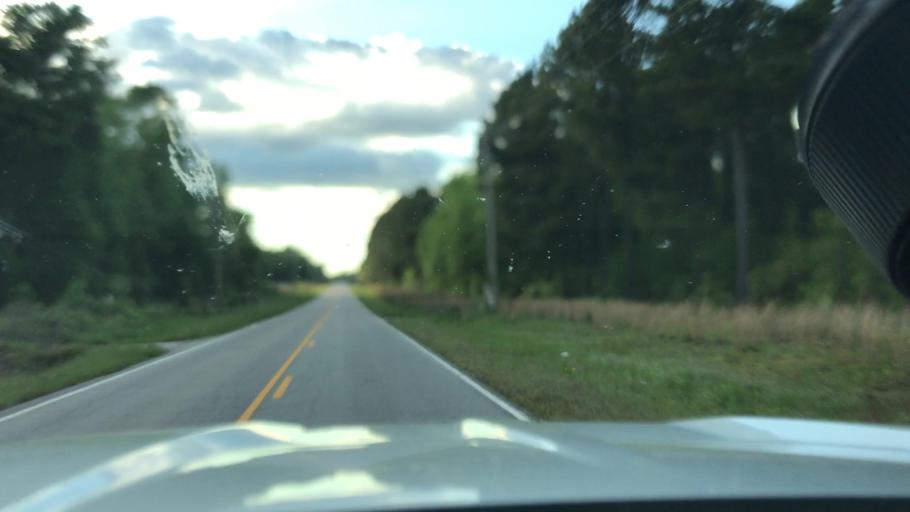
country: US
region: South Carolina
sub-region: Bamberg County
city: Denmark
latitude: 33.4669
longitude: -81.1620
